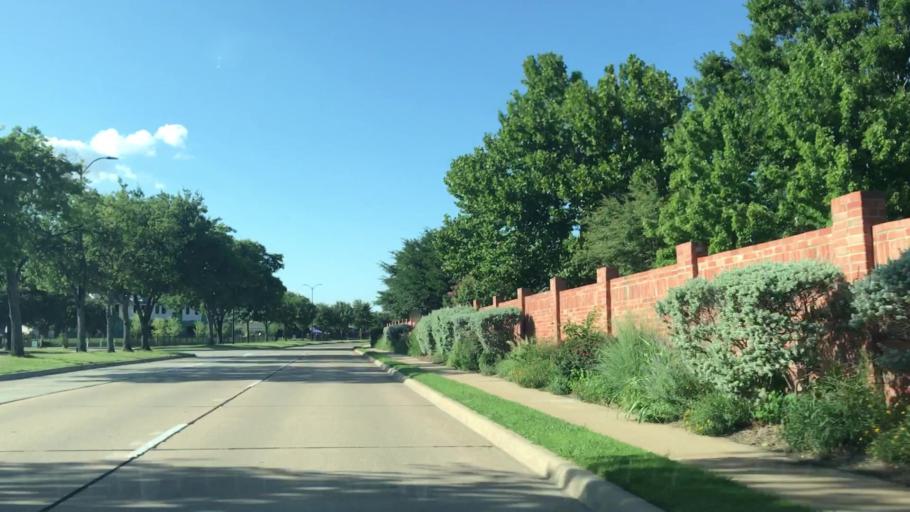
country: US
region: Texas
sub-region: Collin County
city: Frisco
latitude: 33.1271
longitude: -96.7878
